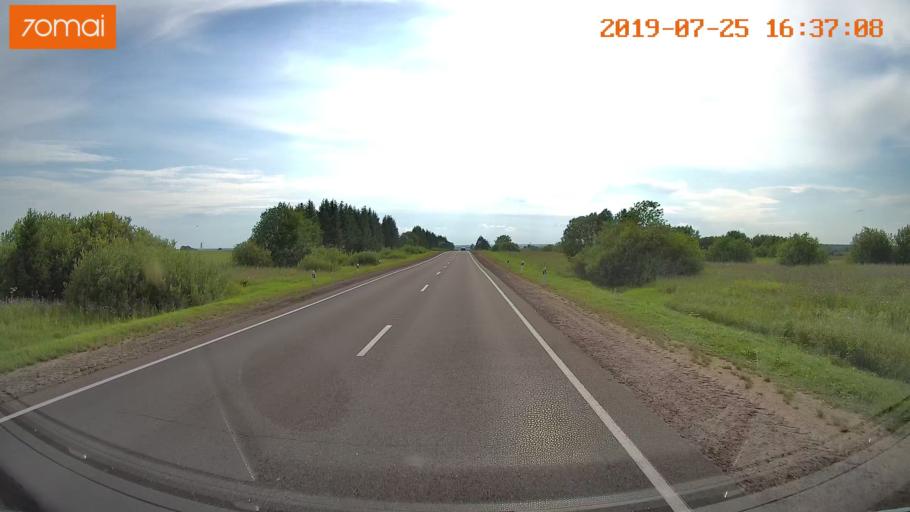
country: RU
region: Ivanovo
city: Privolzhsk
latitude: 57.3921
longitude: 41.3834
